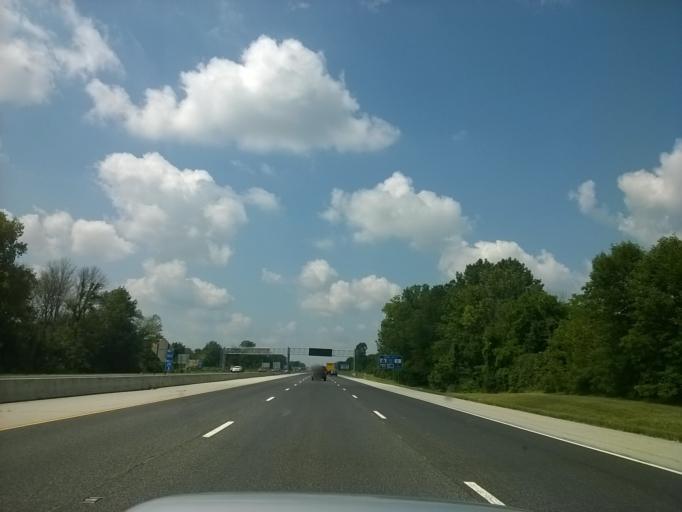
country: US
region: Indiana
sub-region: Marion County
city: Meridian Hills
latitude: 39.9245
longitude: -86.1917
